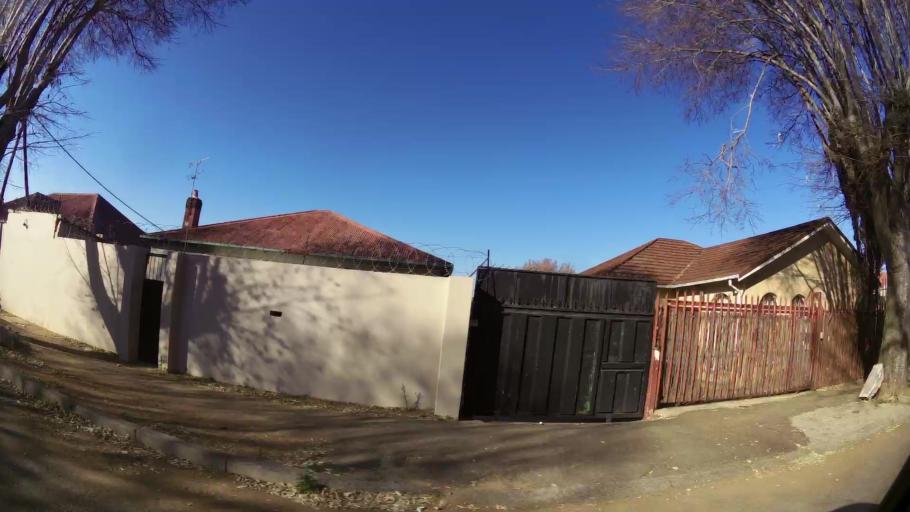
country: ZA
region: Gauteng
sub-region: City of Johannesburg Metropolitan Municipality
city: Johannesburg
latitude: -26.2017
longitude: 28.0992
